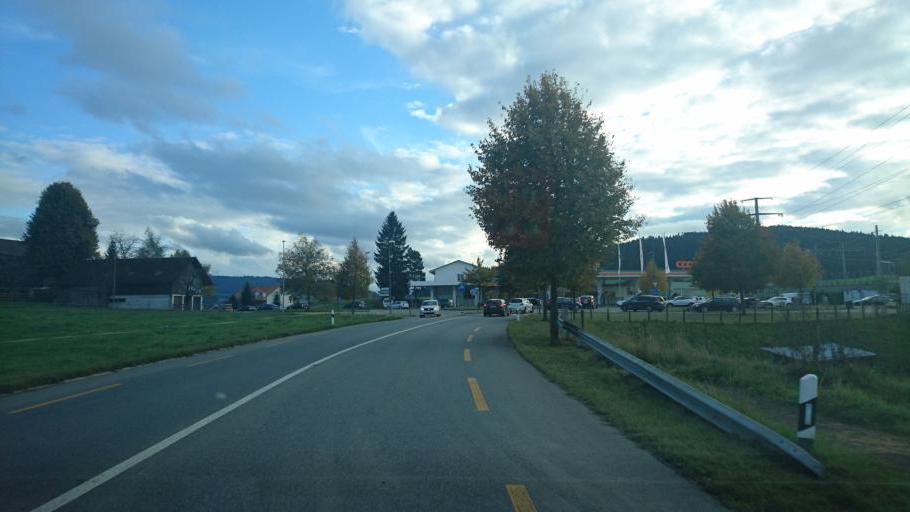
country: CH
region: Bern
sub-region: Bern-Mittelland District
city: Biglen
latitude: 46.9110
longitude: 7.6328
